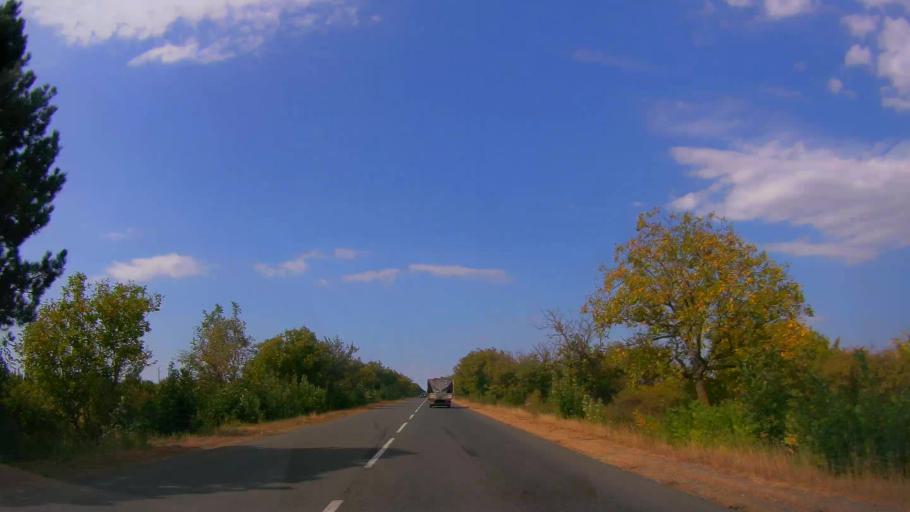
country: BG
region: Burgas
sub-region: Obshtina Aytos
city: Aytos
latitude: 42.6853
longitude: 27.1381
